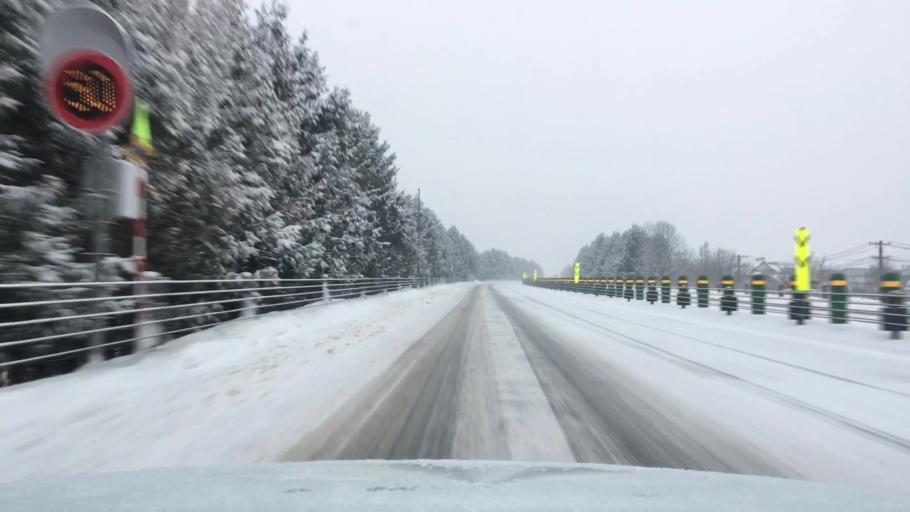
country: JP
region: Akita
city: Hanawa
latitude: 40.2681
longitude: 140.7644
